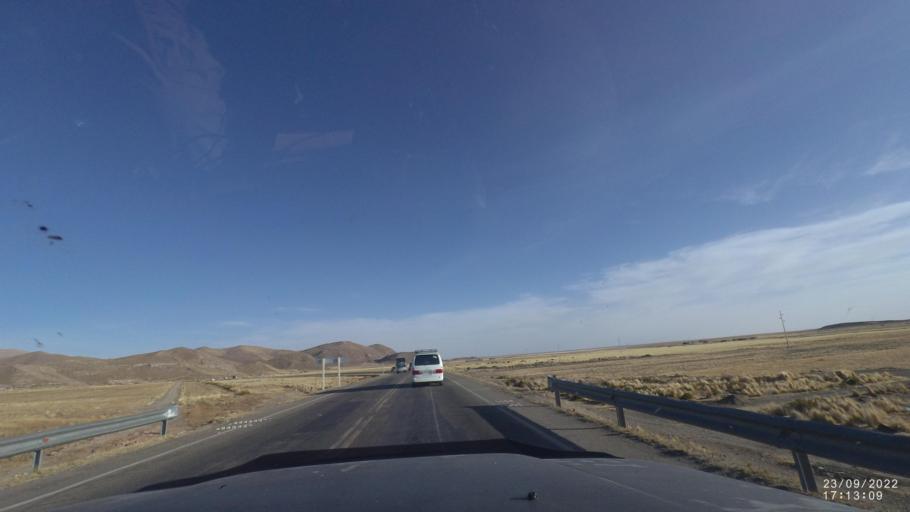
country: BO
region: Oruro
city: Totoral
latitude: -18.7090
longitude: -66.8753
